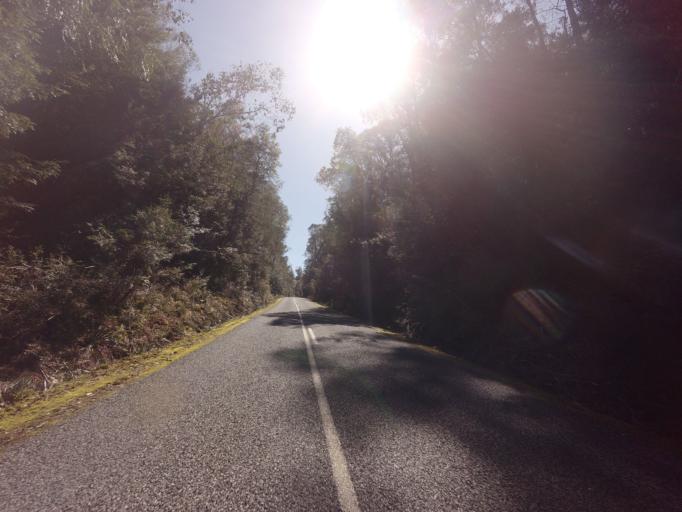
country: AU
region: Tasmania
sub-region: Derwent Valley
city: New Norfolk
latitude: -42.7476
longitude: 146.4135
